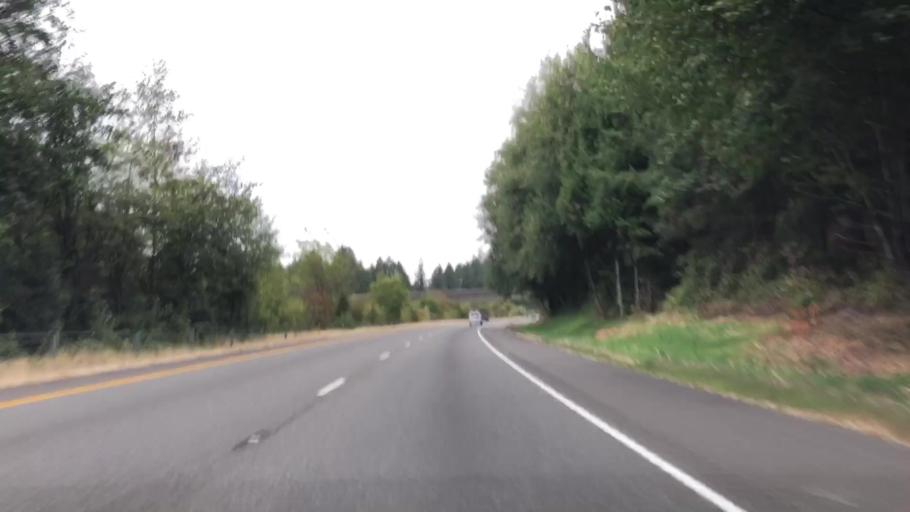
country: US
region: Washington
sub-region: Pierce County
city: Purdy
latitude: 47.4007
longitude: -122.6238
